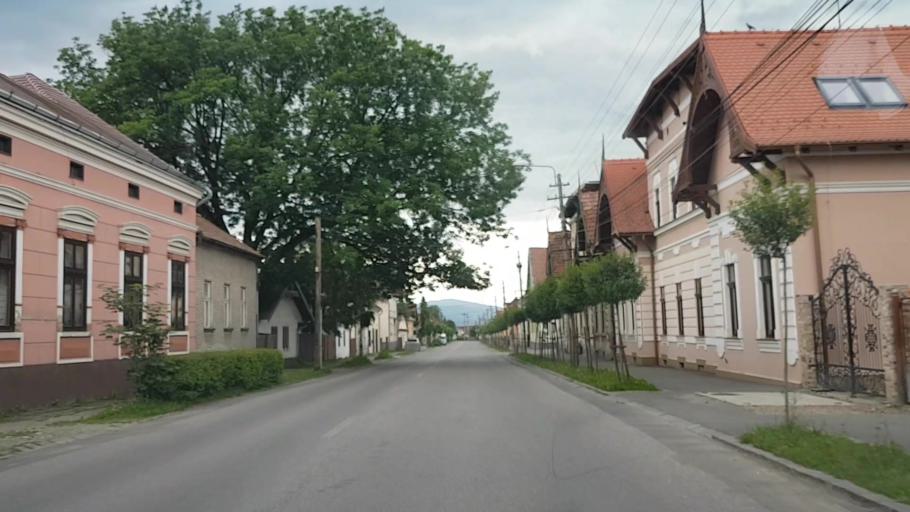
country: RO
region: Harghita
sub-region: Municipiul Gheorgheni
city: Gheorgheni
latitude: 46.7205
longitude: 25.5940
